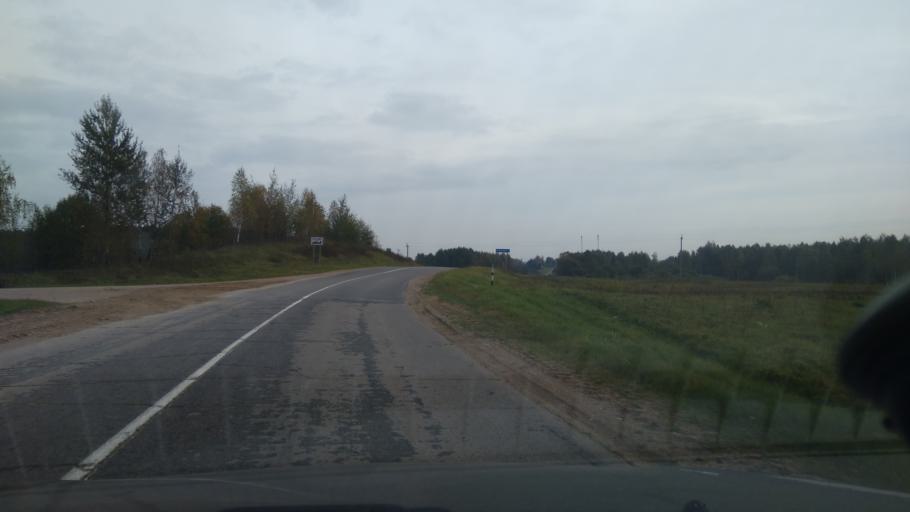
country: BY
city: Michanovichi
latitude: 53.6163
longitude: 27.7267
